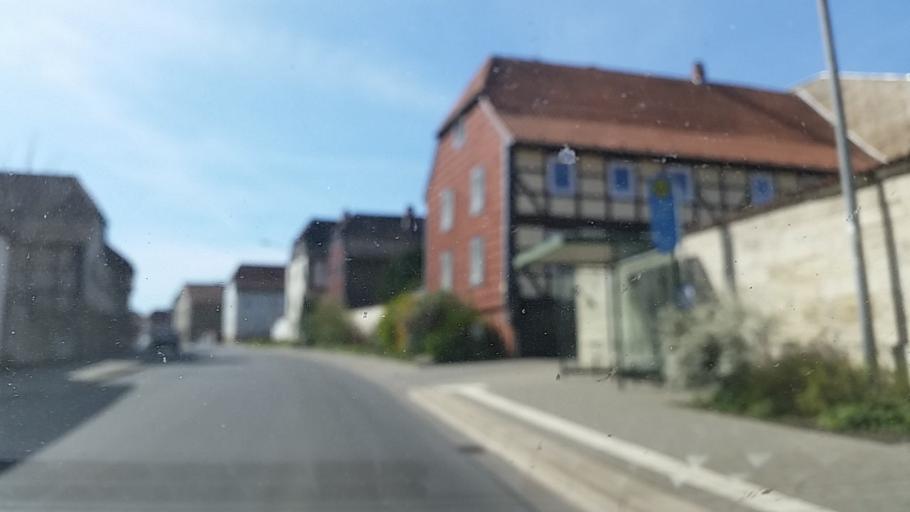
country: DE
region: Lower Saxony
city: Sollingen
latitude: 52.0916
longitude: 10.9244
